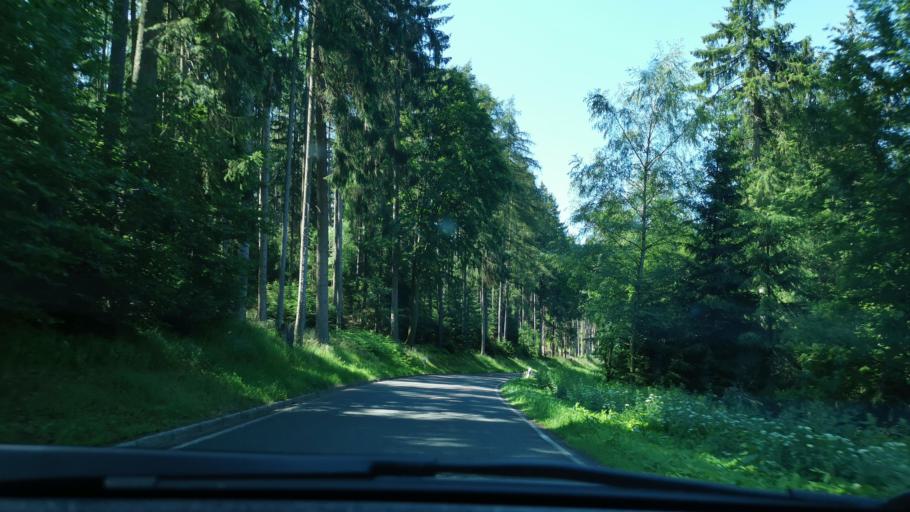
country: DE
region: Hesse
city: Hessisch Lichtenau
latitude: 51.1585
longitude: 9.7513
